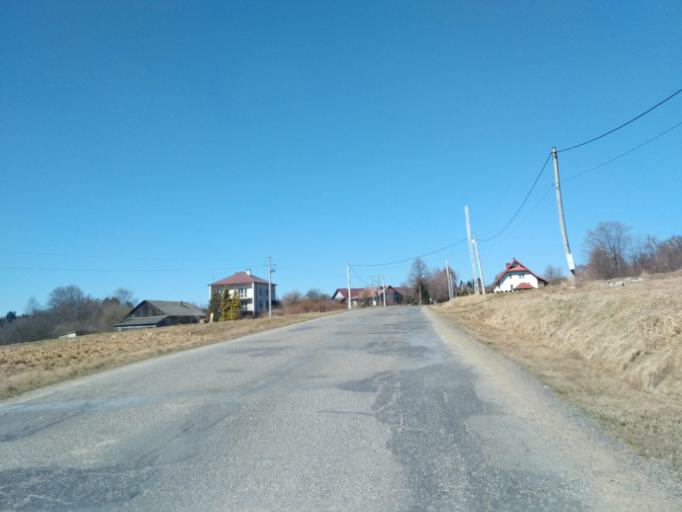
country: PL
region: Subcarpathian Voivodeship
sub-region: Powiat debicki
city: Brzostek
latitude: 49.9435
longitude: 21.4339
